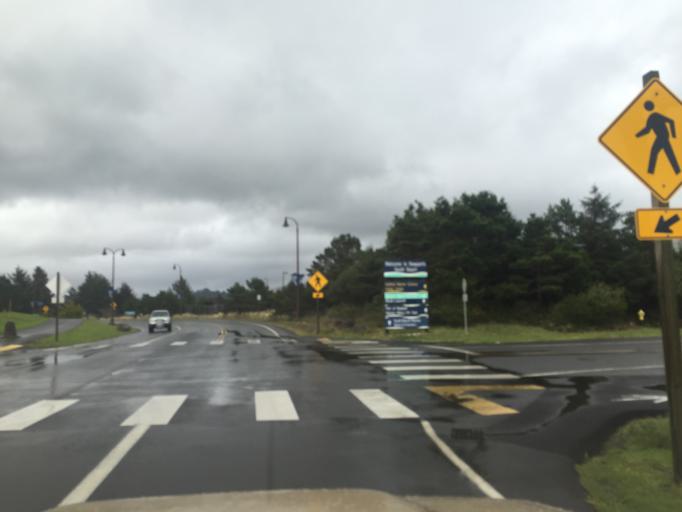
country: US
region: Oregon
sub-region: Lincoln County
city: Newport
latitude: 44.6193
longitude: -124.0501
